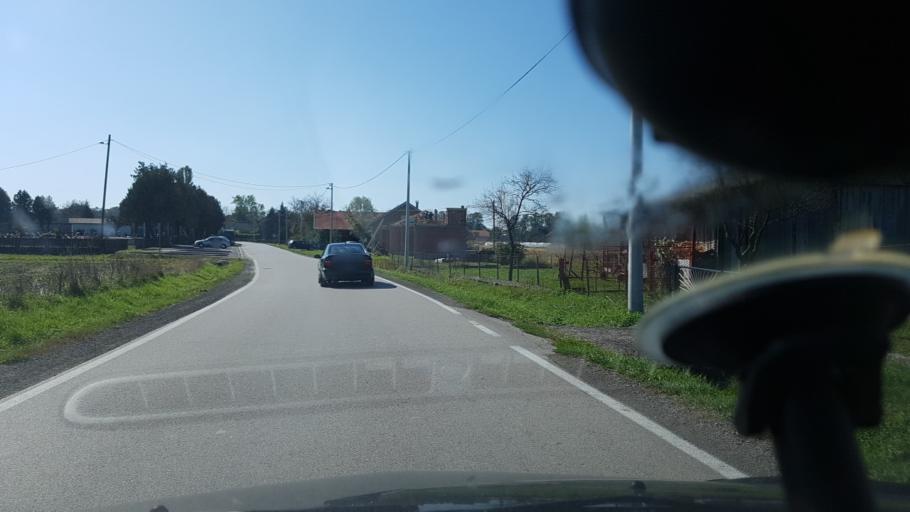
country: HR
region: Zagrebacka
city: Lupoglav
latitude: 45.7407
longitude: 16.3022
